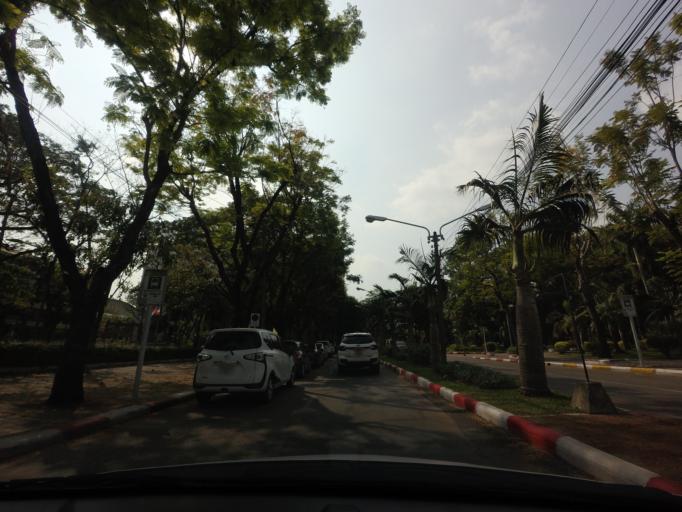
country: TH
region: Bangkok
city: Chatuchak
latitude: 13.8525
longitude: 100.5694
